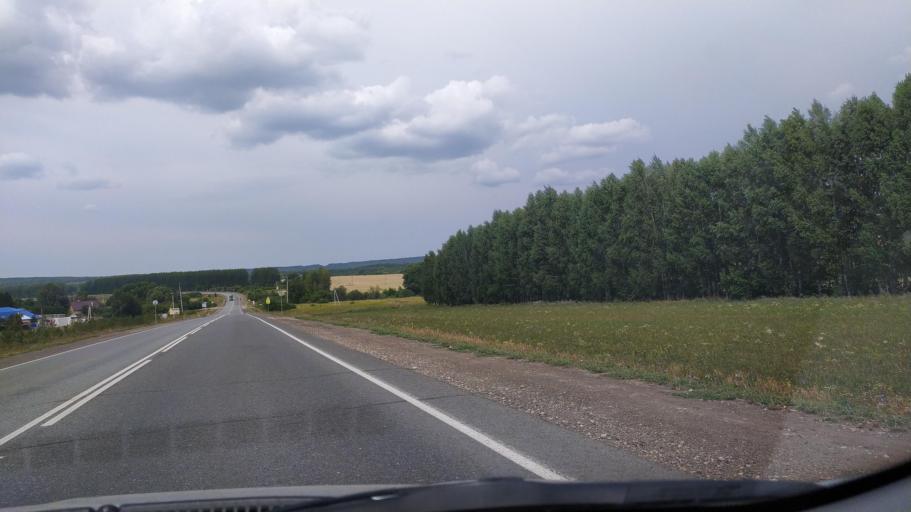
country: RU
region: Tatarstan
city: Al'met'yevsk
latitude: 54.9015
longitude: 52.2071
